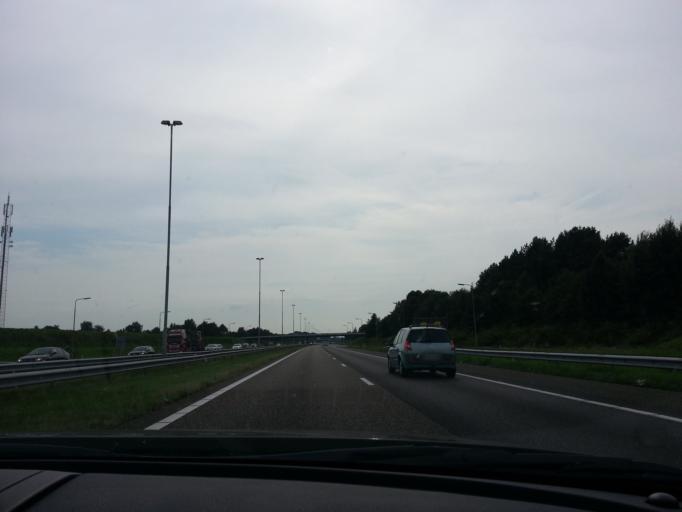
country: NL
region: North Brabant
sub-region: Gemeente Breda
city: Breda
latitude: 51.5361
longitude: 4.7953
